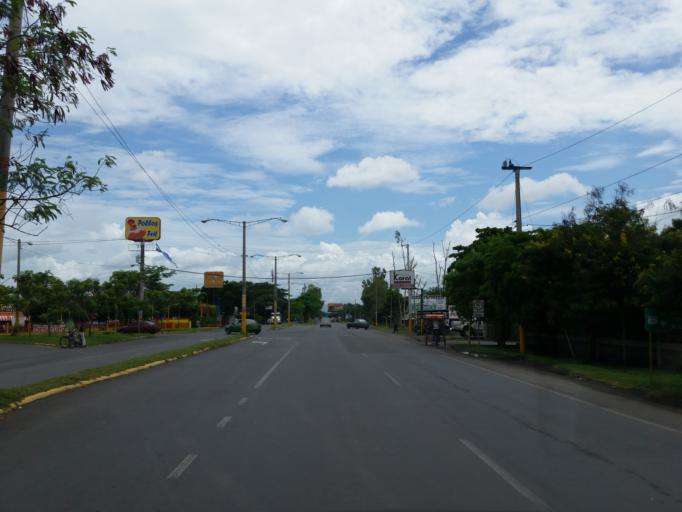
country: NI
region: Managua
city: Tipitapa
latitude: 12.1958
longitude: -86.1042
